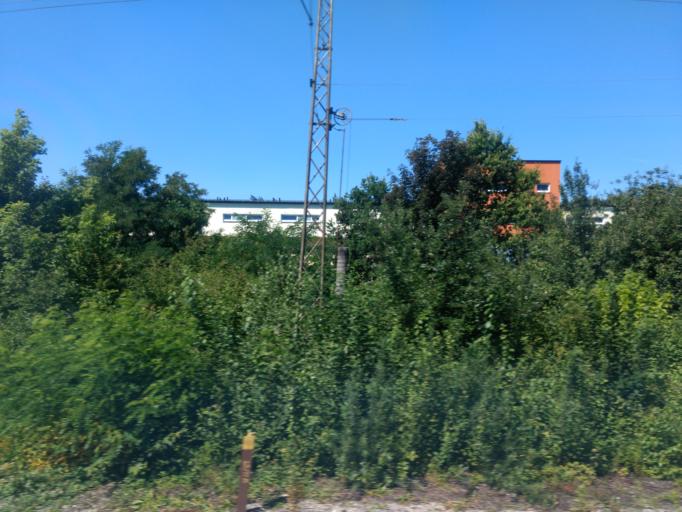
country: DE
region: Bavaria
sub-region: Upper Bavaria
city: Unterfoehring
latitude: 48.1613
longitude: 11.6478
